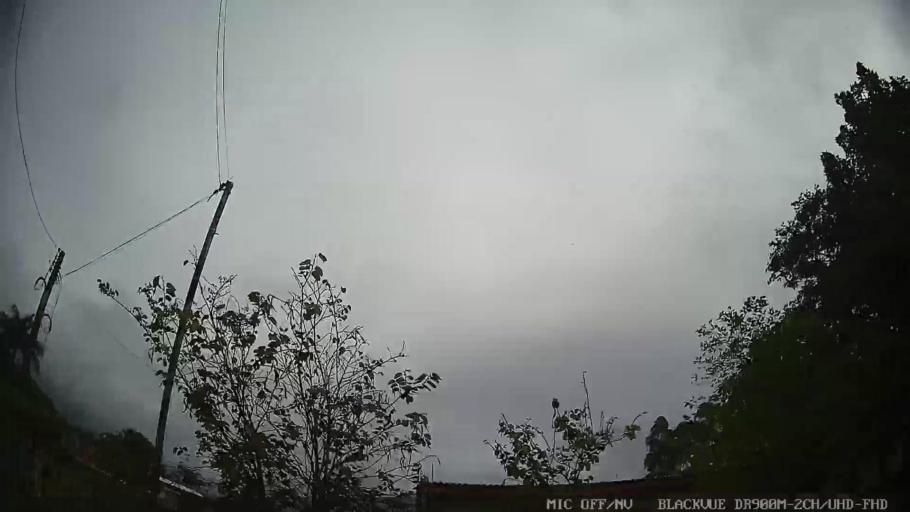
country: BR
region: Sao Paulo
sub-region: Osasco
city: Osasco
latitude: -23.4838
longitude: -46.7298
